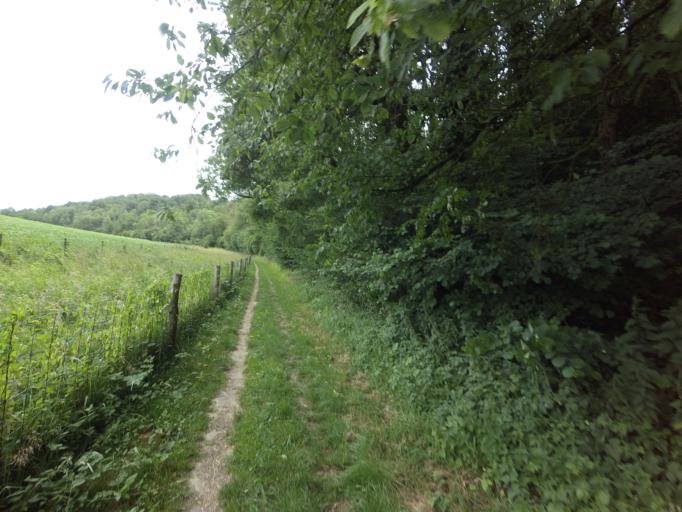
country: NL
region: Limburg
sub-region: Valkenburg aan de Geul
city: Schin op Geul
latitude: 50.8412
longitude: 5.8559
